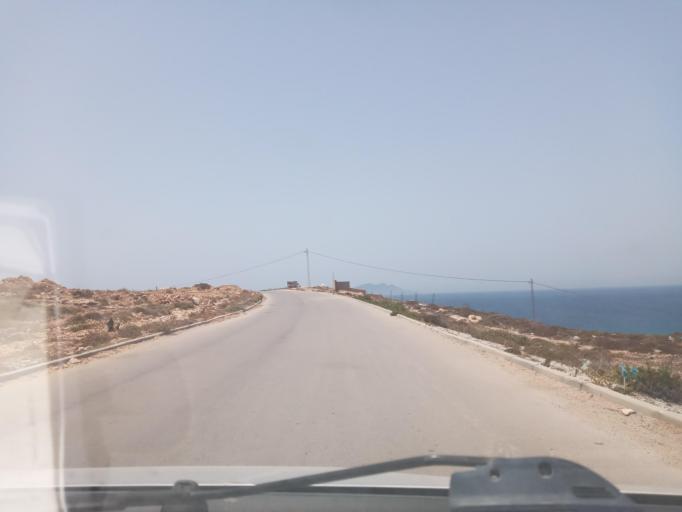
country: TN
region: Nabul
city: El Haouaria
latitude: 37.0557
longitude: 10.9956
